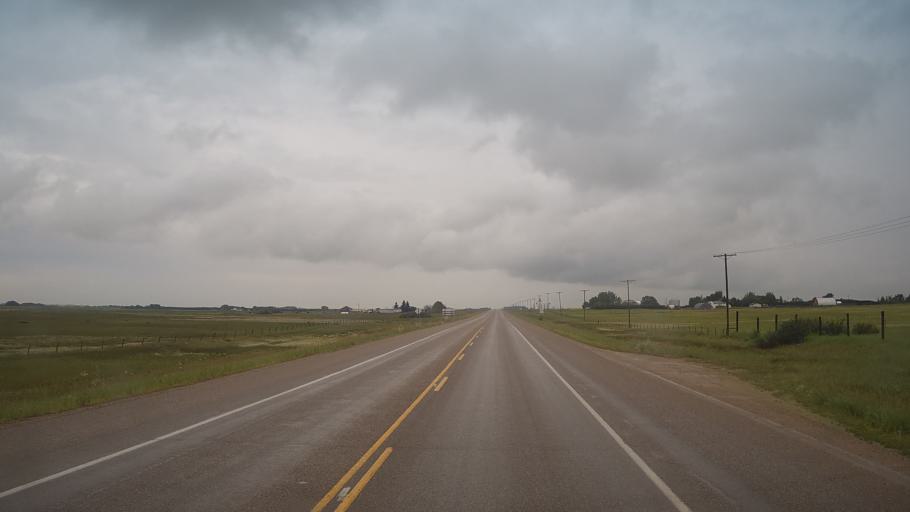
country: CA
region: Saskatchewan
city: Wilkie
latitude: 52.4057
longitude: -108.7271
